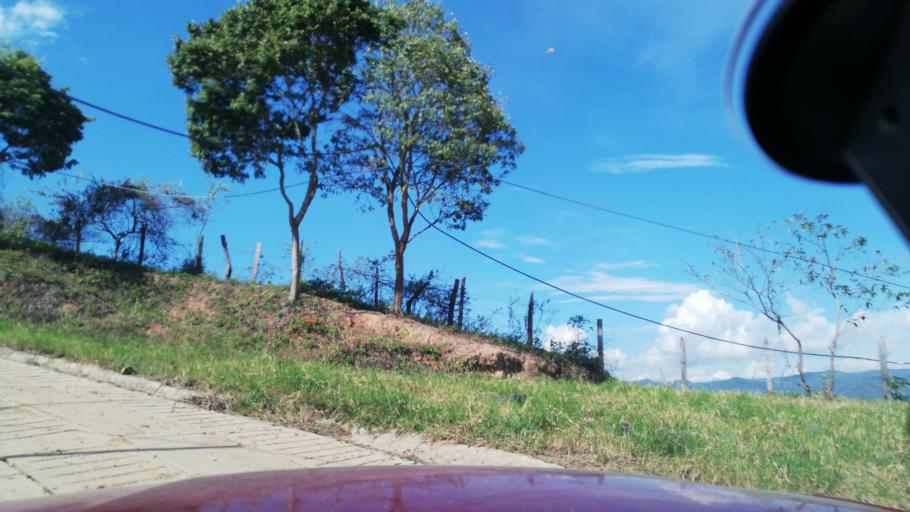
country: CO
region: Cundinamarca
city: Quipile
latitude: 4.7432
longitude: -74.6151
